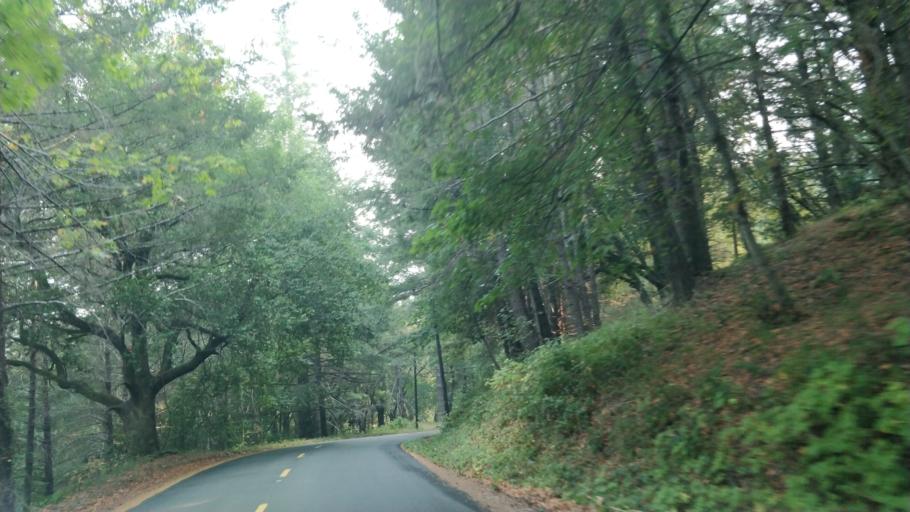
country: US
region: California
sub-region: Humboldt County
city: Rio Dell
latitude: 40.2885
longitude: -124.2533
